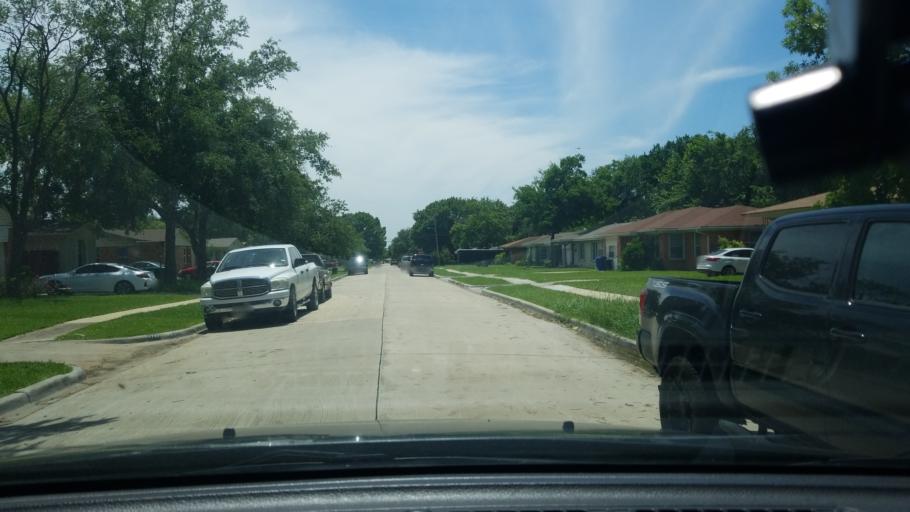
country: US
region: Texas
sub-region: Dallas County
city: Mesquite
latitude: 32.7886
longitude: -96.6121
